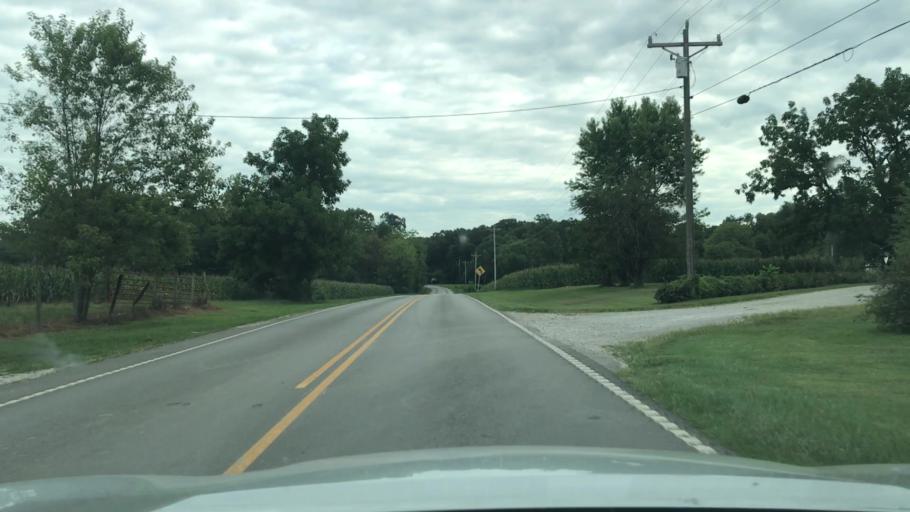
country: US
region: Kentucky
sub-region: Todd County
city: Guthrie
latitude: 36.7219
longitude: -87.1903
